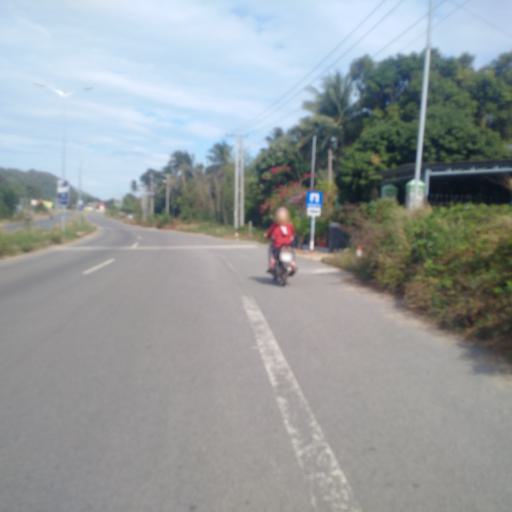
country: VN
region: Kien Giang
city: Duong GJong
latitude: 10.1106
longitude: 104.0142
